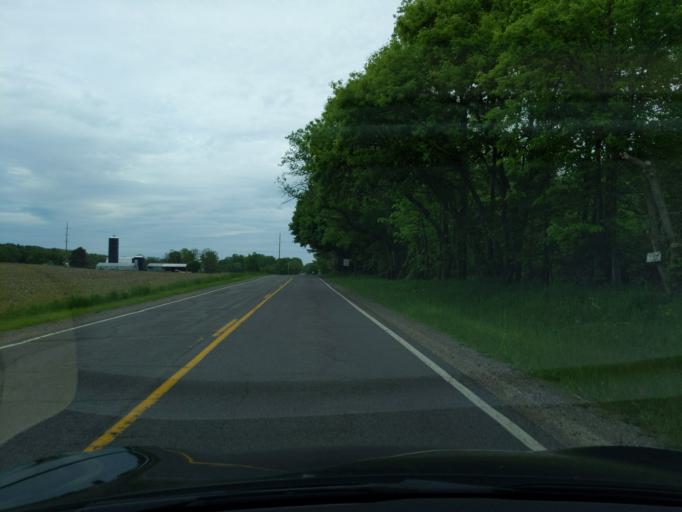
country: US
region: Michigan
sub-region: Ingham County
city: Leslie
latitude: 42.4980
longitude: -84.3562
